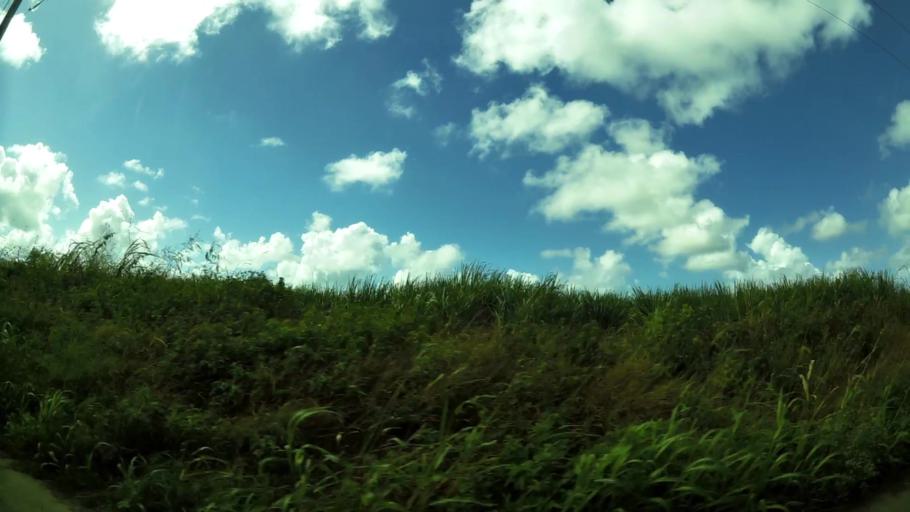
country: GP
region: Guadeloupe
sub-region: Guadeloupe
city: Petit-Canal
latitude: 16.4196
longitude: -61.4729
